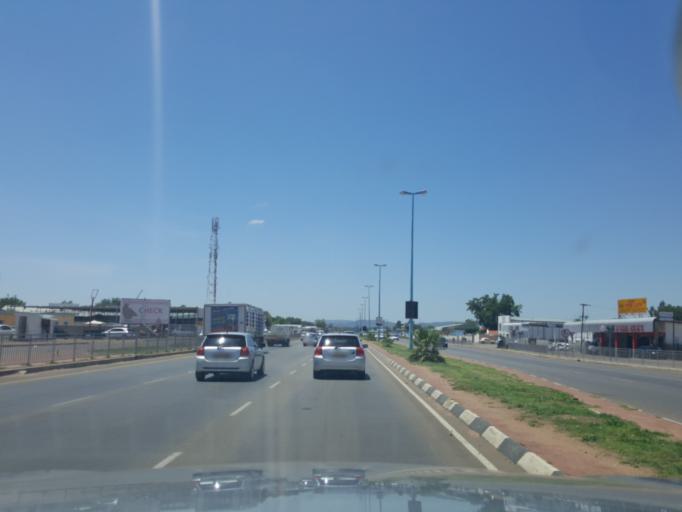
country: BW
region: Kweneng
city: Mogoditshane
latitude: -24.6227
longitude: 25.8679
